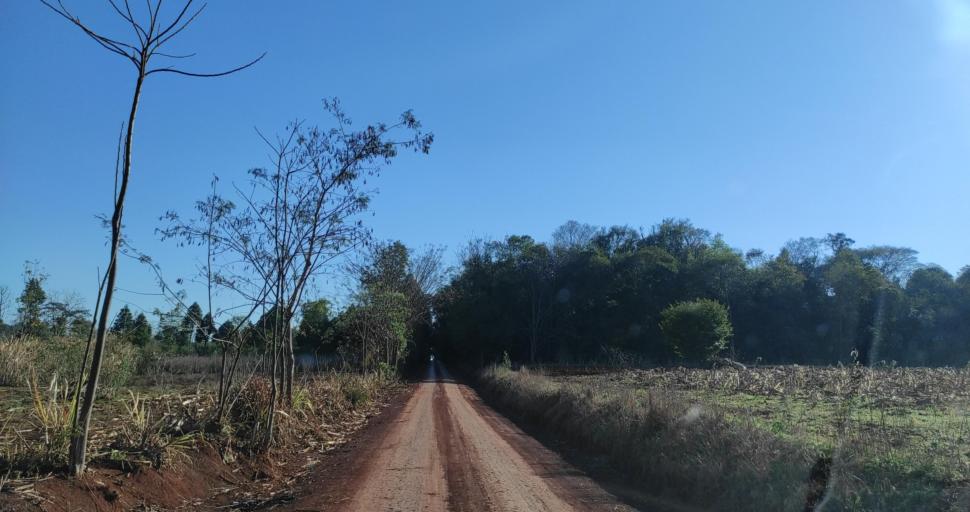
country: AR
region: Misiones
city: Capiovi
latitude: -26.8789
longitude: -55.0165
